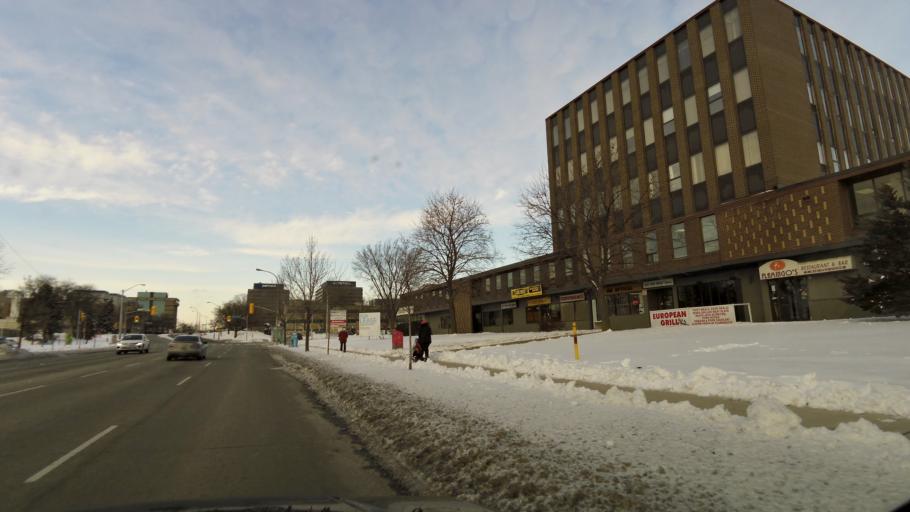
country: CA
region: Ontario
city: Etobicoke
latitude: 43.6414
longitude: -79.5655
